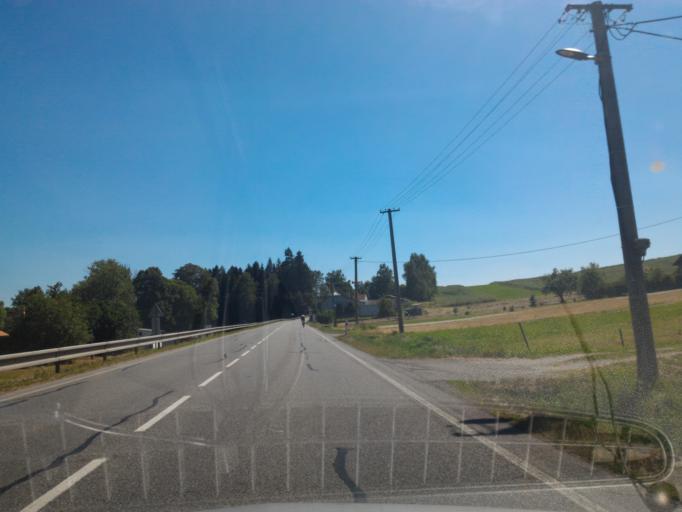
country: CZ
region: Vysocina
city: Dolni Cerekev
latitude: 49.3307
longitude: 15.4845
